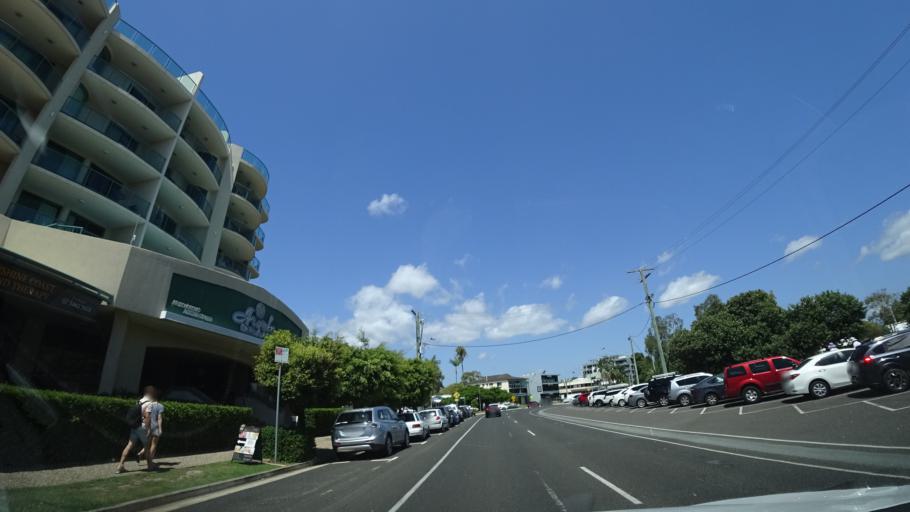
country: AU
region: Queensland
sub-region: Sunshine Coast
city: Mooloolaba
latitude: -26.6548
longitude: 153.0996
